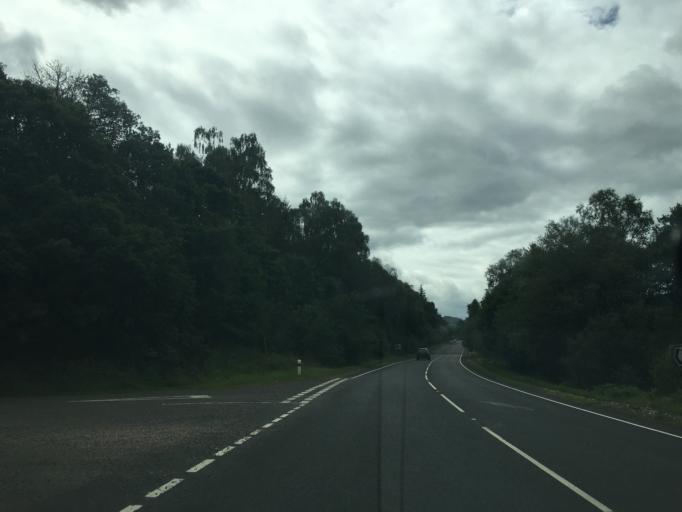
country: GB
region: Scotland
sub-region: Stirling
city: Callander
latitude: 56.3765
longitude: -4.2861
